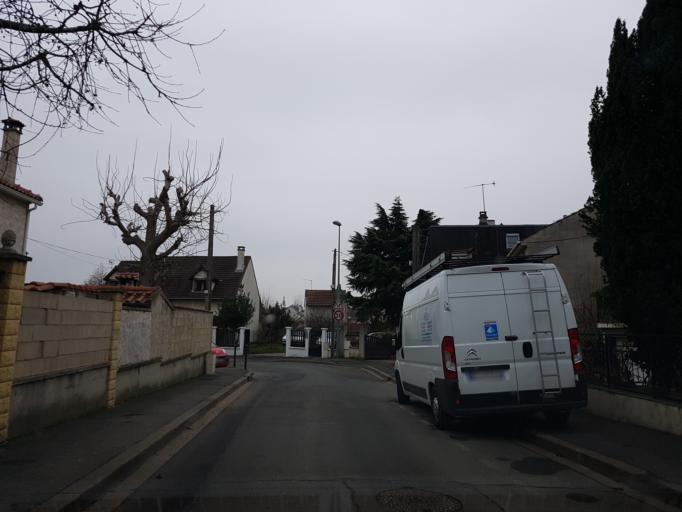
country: FR
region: Ile-de-France
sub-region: Departement du Val-de-Marne
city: Villejuif
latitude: 48.7945
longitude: 2.3783
